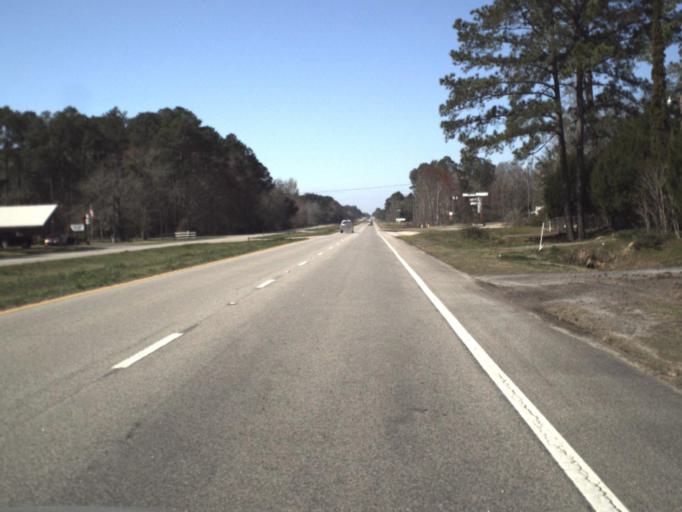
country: US
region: Florida
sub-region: Jackson County
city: Sneads
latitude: 30.7191
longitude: -84.9987
